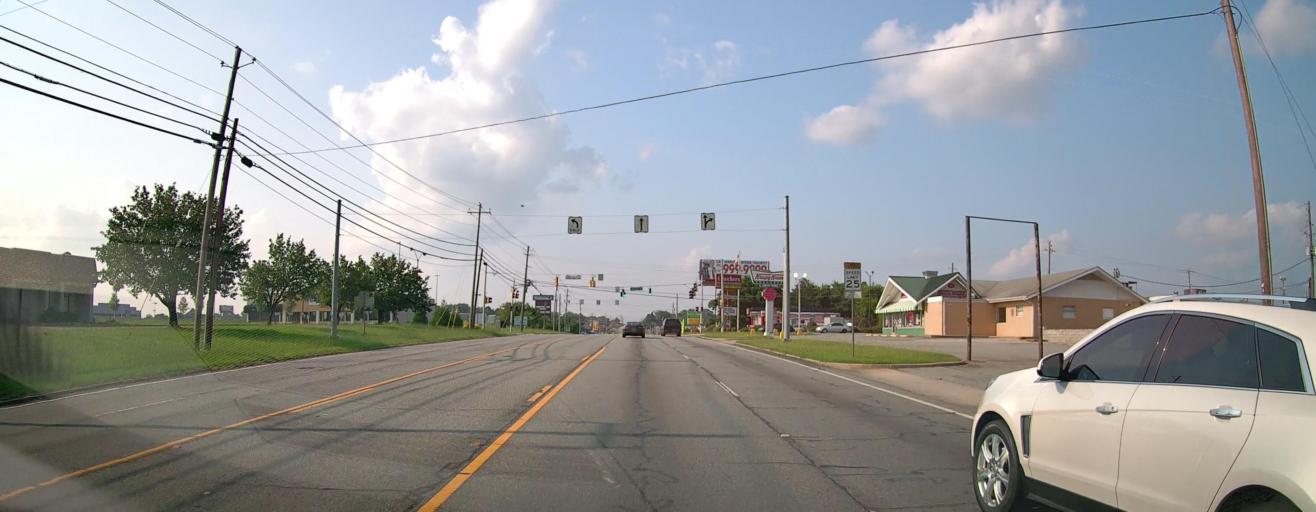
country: US
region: Georgia
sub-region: Bibb County
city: Macon
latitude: 32.8104
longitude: -83.6629
